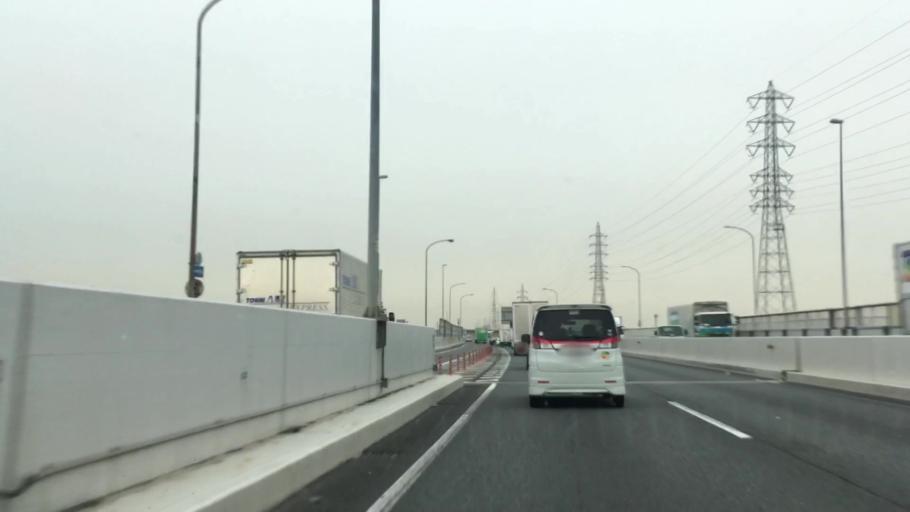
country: JP
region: Aichi
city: Chiryu
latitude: 35.0013
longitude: 137.0284
